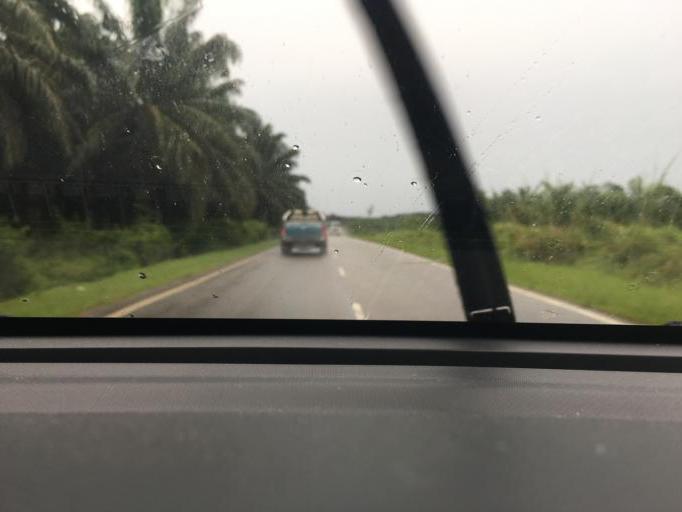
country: MY
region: Kedah
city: Bedong
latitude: 5.6583
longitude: 100.6315
